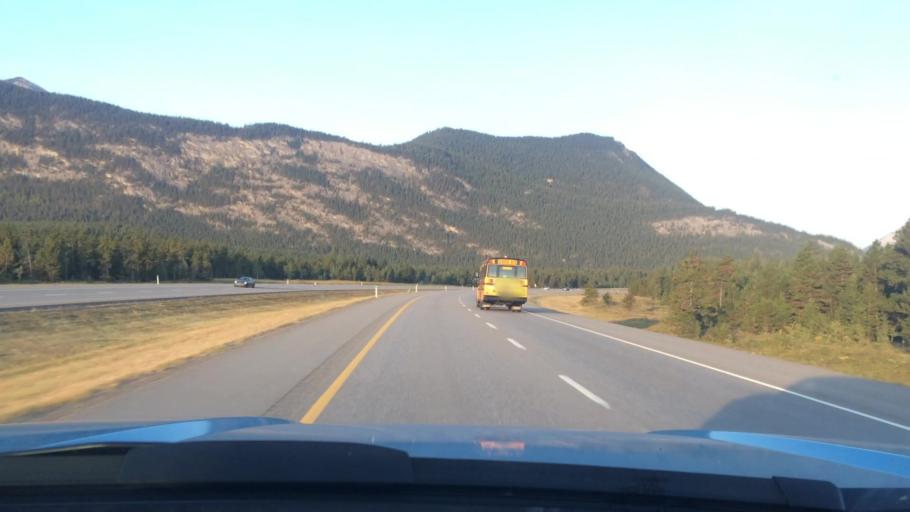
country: CA
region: Alberta
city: Canmore
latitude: 51.0678
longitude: -115.0837
